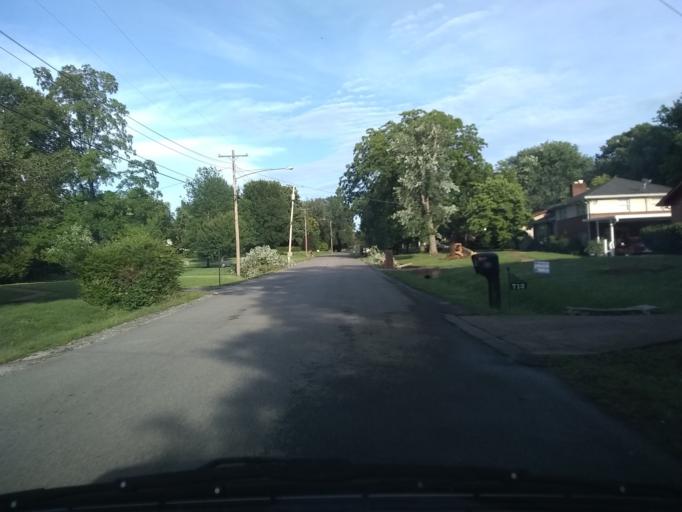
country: US
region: Tennessee
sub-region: Davidson County
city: Oak Hill
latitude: 36.1200
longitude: -86.7088
